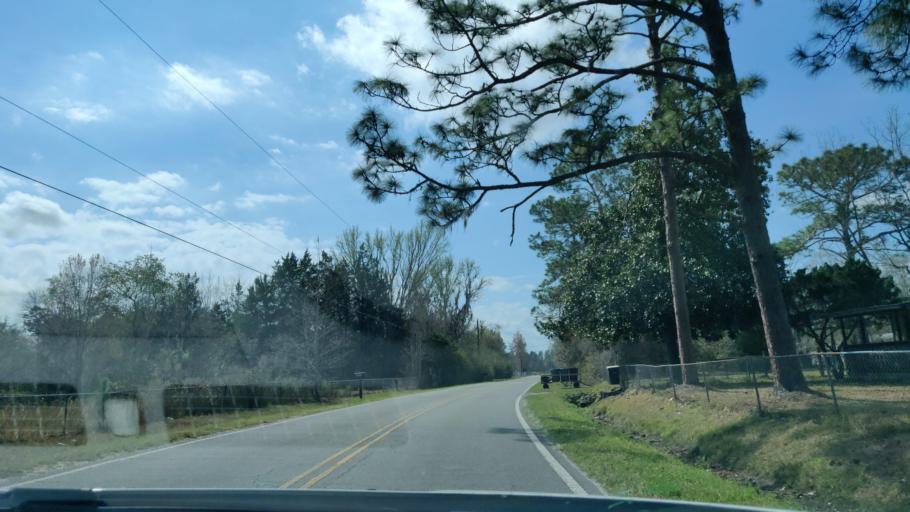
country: US
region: Florida
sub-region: Duval County
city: Baldwin
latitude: 30.1930
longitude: -81.9662
